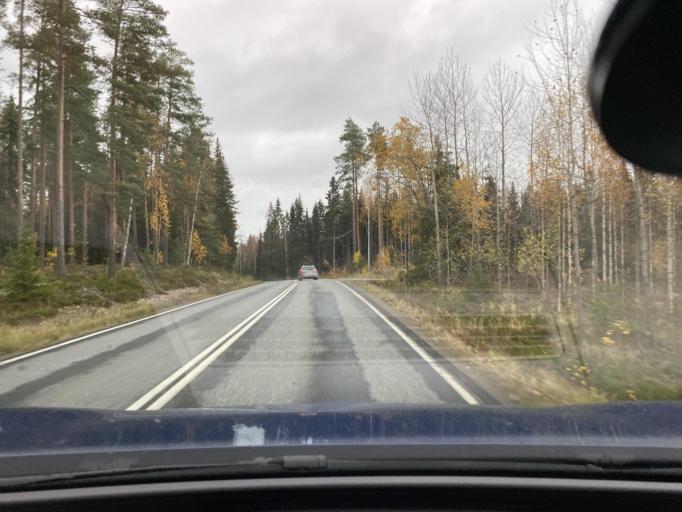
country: FI
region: Satakunta
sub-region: Pori
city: Huittinen
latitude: 61.1056
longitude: 22.5622
